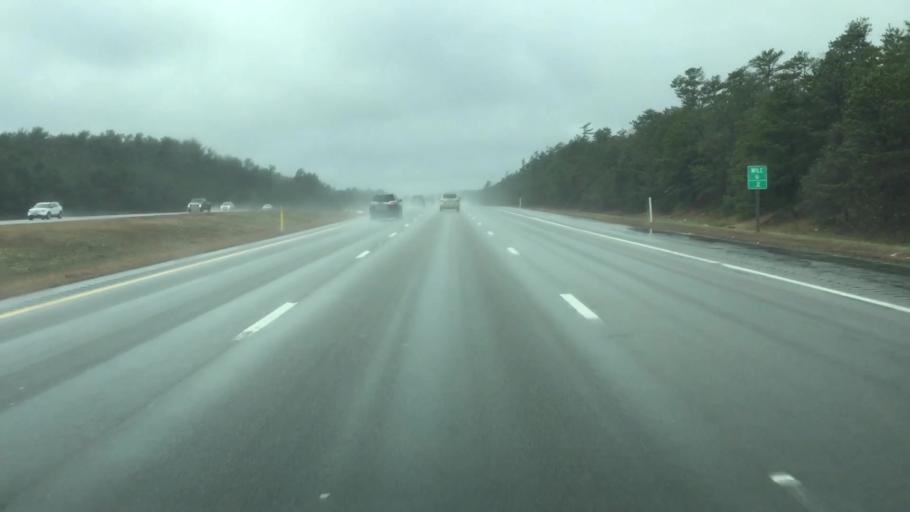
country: US
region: Massachusetts
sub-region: Plymouth County
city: White Island Shores
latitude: 41.7798
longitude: -70.6224
